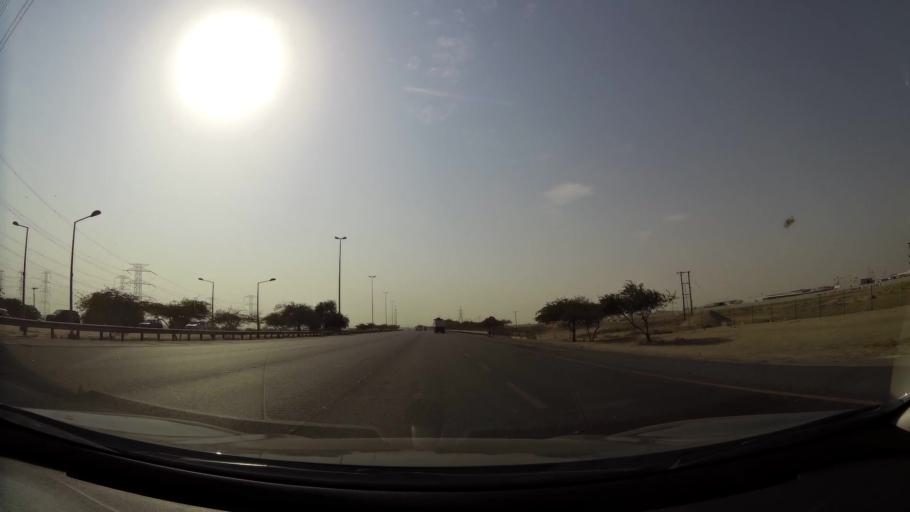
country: KW
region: Al Ahmadi
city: Al Ahmadi
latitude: 29.0018
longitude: 48.0964
